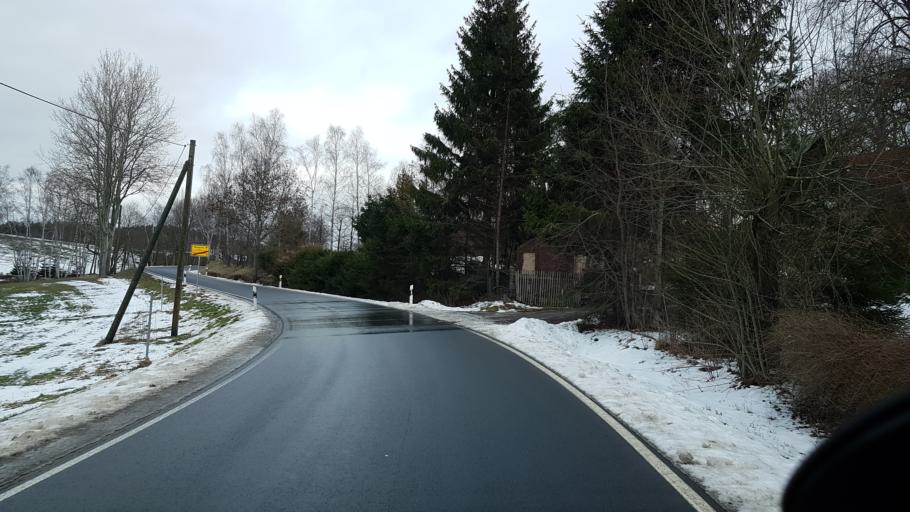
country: DE
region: Saxony
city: Kirchberg
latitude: 50.6332
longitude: 12.5274
